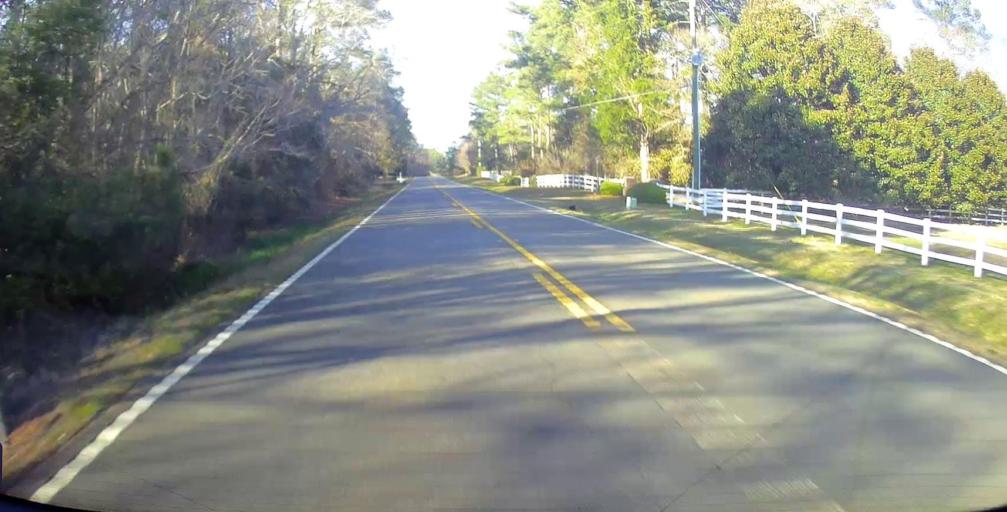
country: US
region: Georgia
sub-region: Sumter County
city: Americus
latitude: 32.0239
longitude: -84.2193
